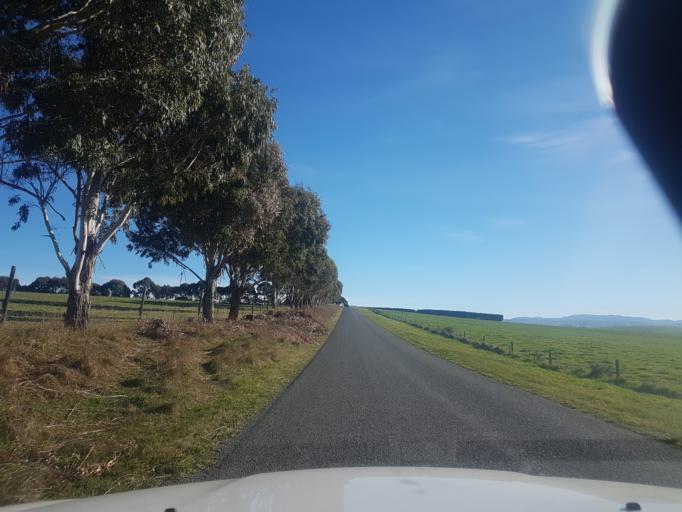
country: NZ
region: Canterbury
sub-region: Timaru District
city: Pleasant Point
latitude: -44.2475
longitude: 171.0784
